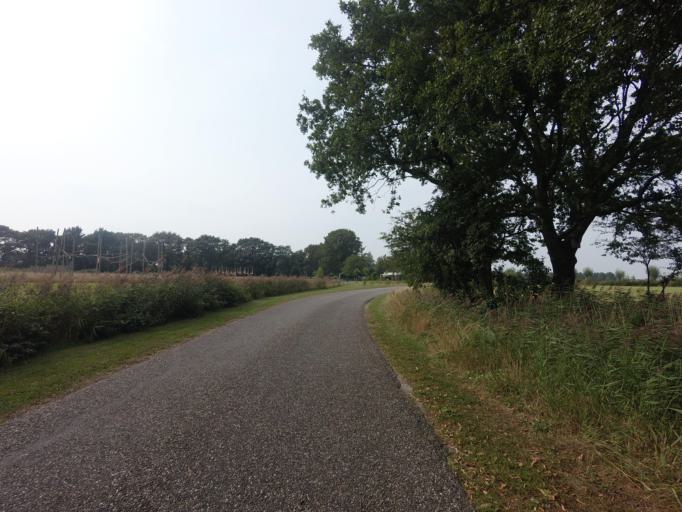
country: NL
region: Drenthe
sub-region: Gemeente Tynaarlo
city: Vries
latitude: 53.1157
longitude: 6.5387
